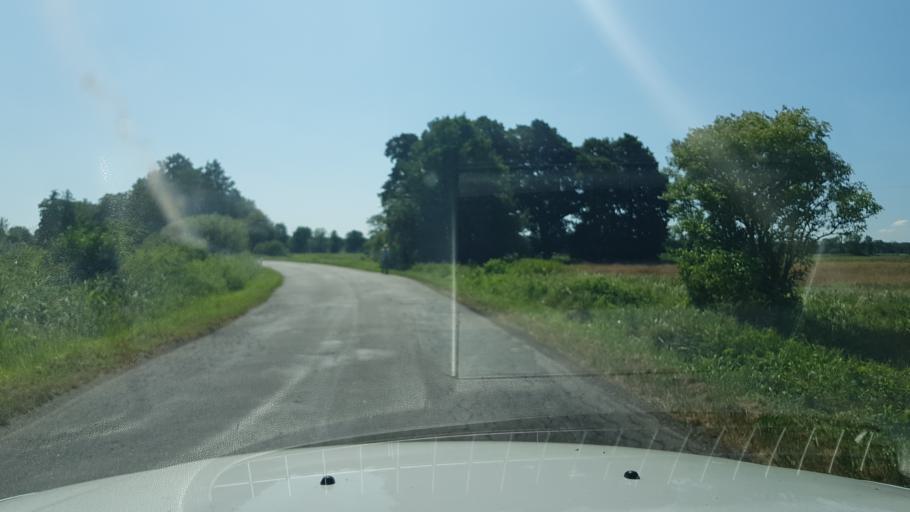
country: PL
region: West Pomeranian Voivodeship
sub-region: Powiat goleniowski
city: Goleniow
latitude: 53.4564
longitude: 14.7313
